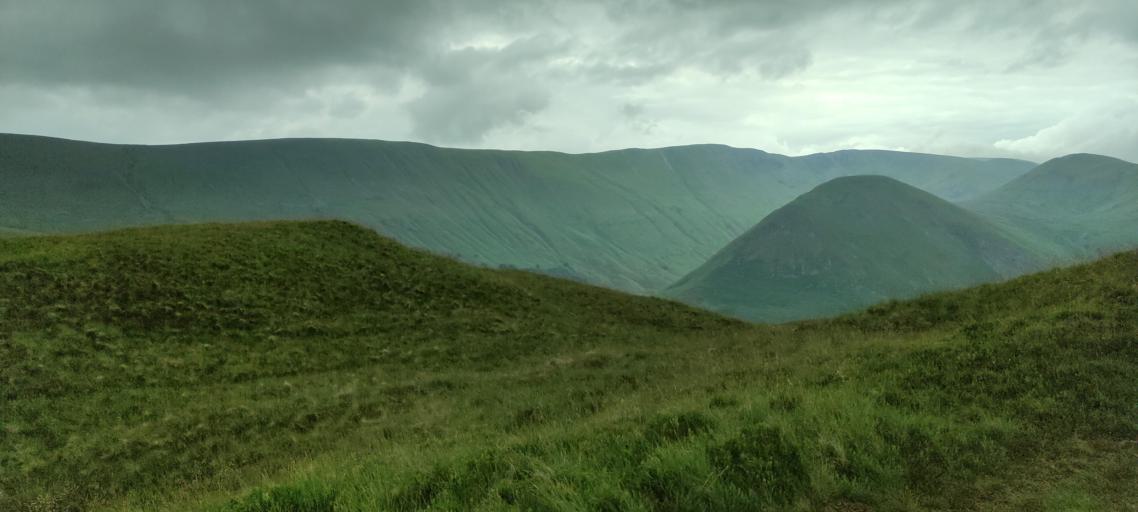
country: GB
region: England
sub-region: Cumbria
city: Ambleside
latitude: 54.5456
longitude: -2.8858
